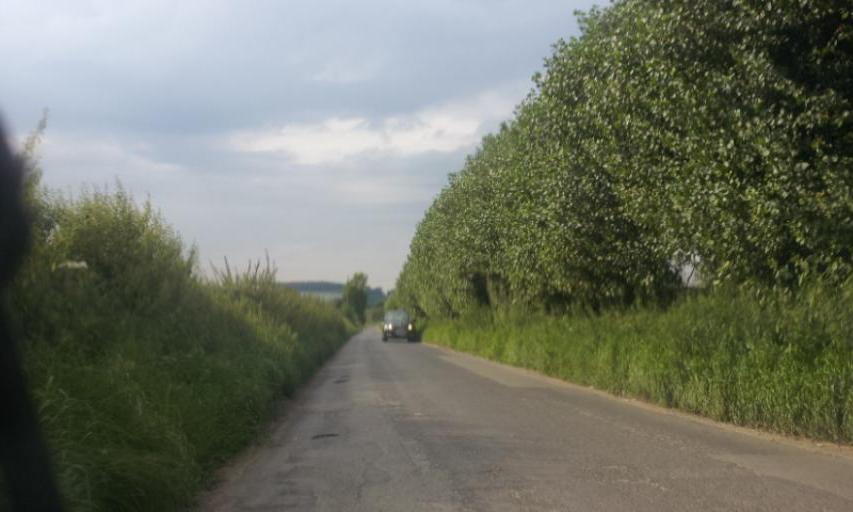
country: GB
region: England
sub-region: Kent
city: Yalding
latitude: 51.2294
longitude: 0.4279
